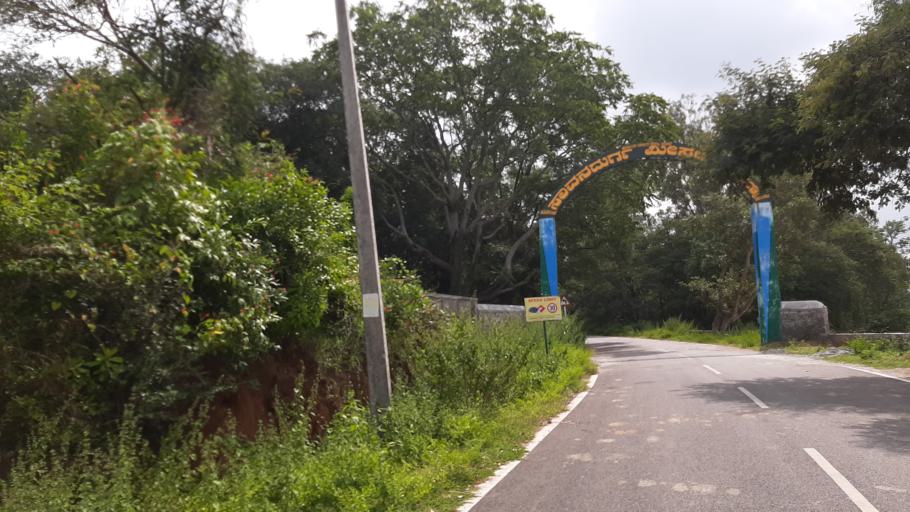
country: IN
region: Karnataka
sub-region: Ramanagara
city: Magadi
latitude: 12.9025
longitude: 77.2890
